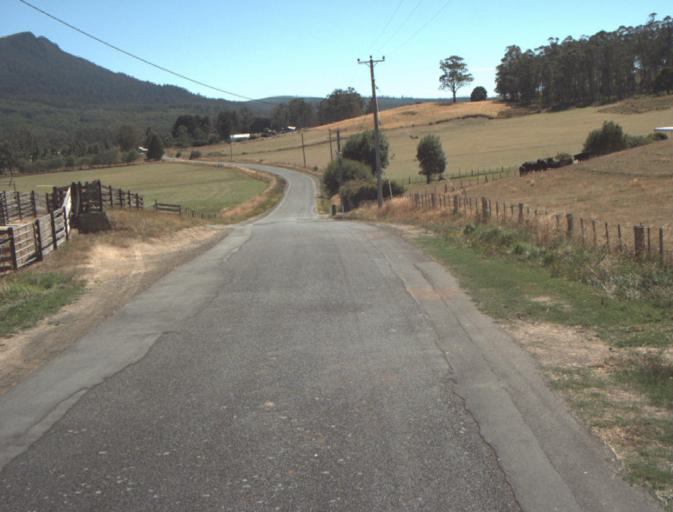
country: AU
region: Tasmania
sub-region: Launceston
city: Newstead
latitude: -41.3451
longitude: 147.3031
